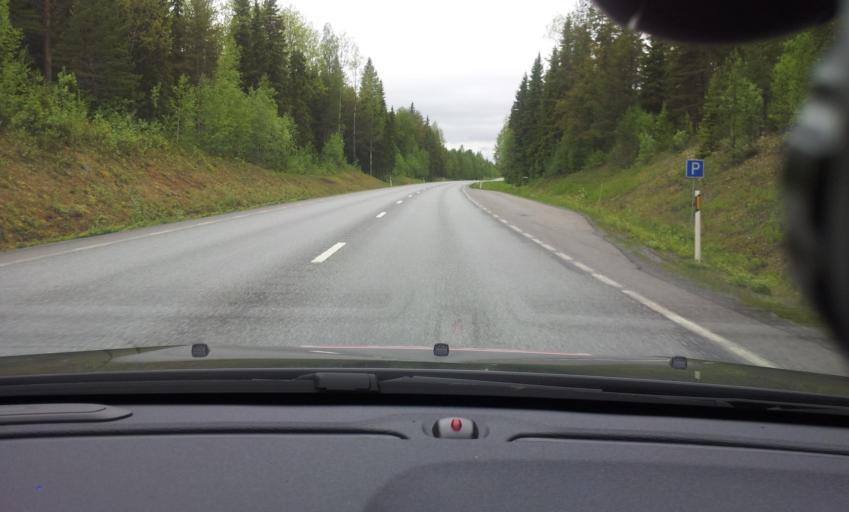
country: SE
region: Jaemtland
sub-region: Krokoms Kommun
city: Krokom
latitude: 63.3212
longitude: 14.2237
